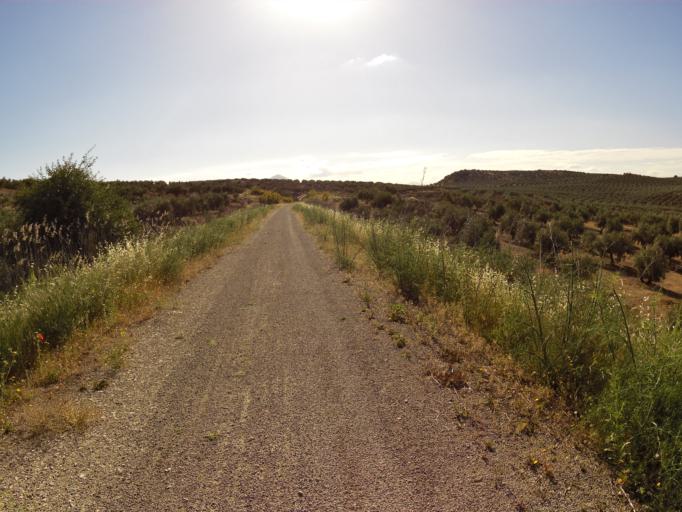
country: ES
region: Andalusia
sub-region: Province of Cordoba
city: Luque
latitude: 37.5835
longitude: -4.2023
